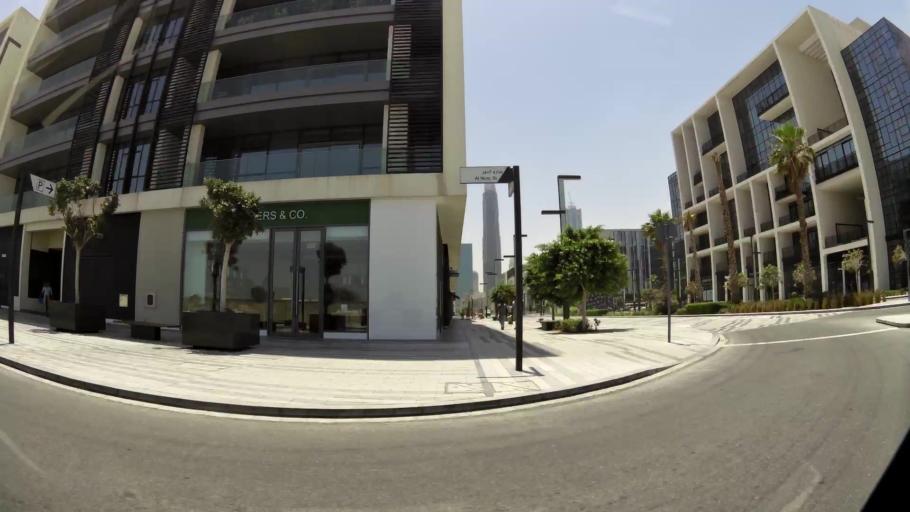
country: AE
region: Dubai
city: Dubai
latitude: 25.2038
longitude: 55.2613
